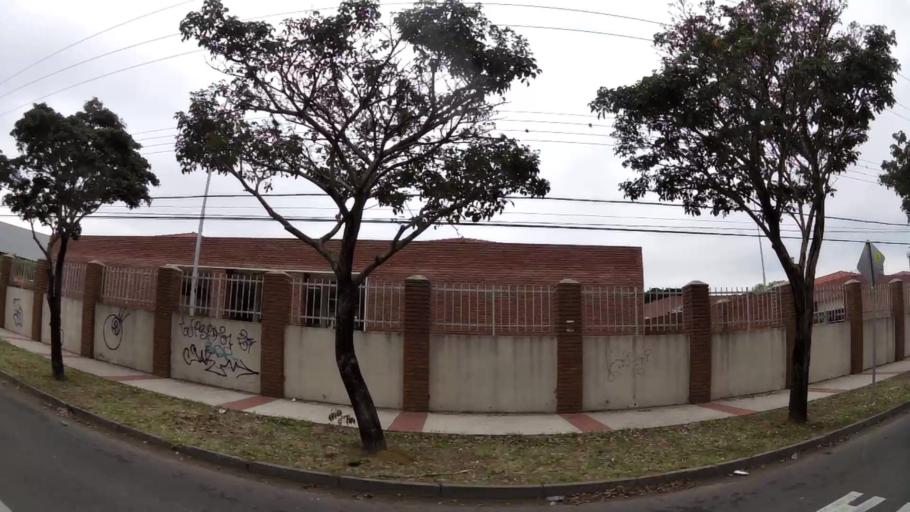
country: BO
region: Santa Cruz
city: Santa Cruz de la Sierra
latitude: -17.7615
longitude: -63.1890
